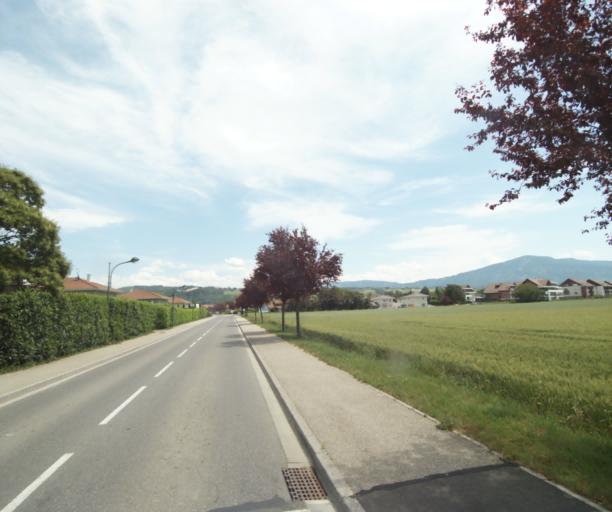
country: FR
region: Rhone-Alpes
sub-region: Departement de la Haute-Savoie
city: Douvaine
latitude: 46.3075
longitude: 6.2918
